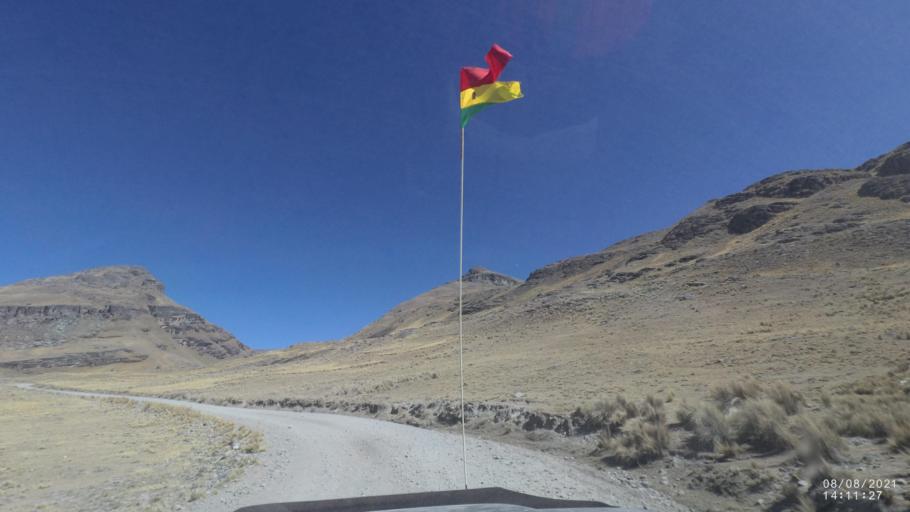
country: BO
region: Cochabamba
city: Sipe Sipe
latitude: -17.1593
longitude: -66.4312
